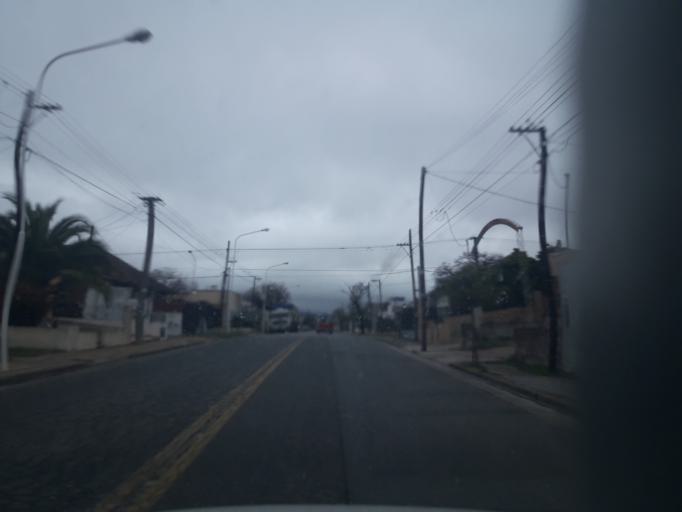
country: AR
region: Buenos Aires
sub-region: Partido de Tandil
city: Tandil
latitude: -37.3126
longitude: -59.1547
